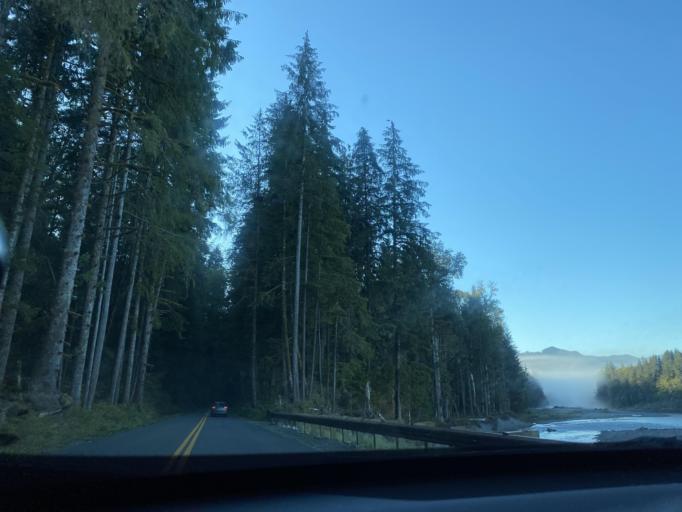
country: US
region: Washington
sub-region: Clallam County
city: Forks
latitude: 47.8168
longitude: -124.1108
